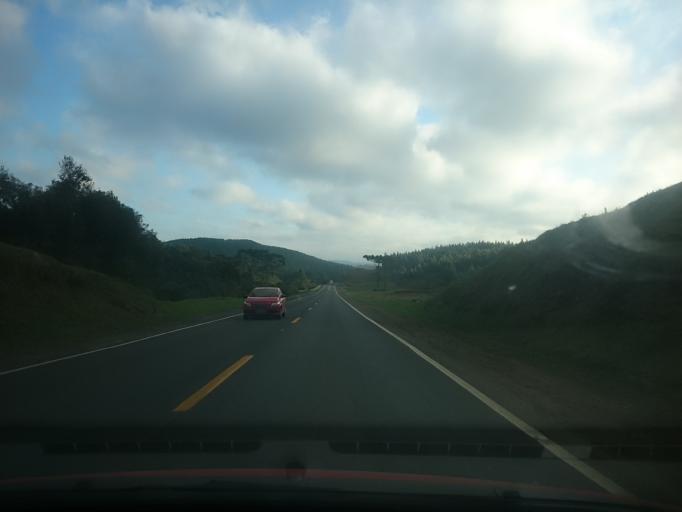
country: BR
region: Santa Catarina
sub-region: Lages
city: Lages
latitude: -28.0493
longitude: -50.5683
